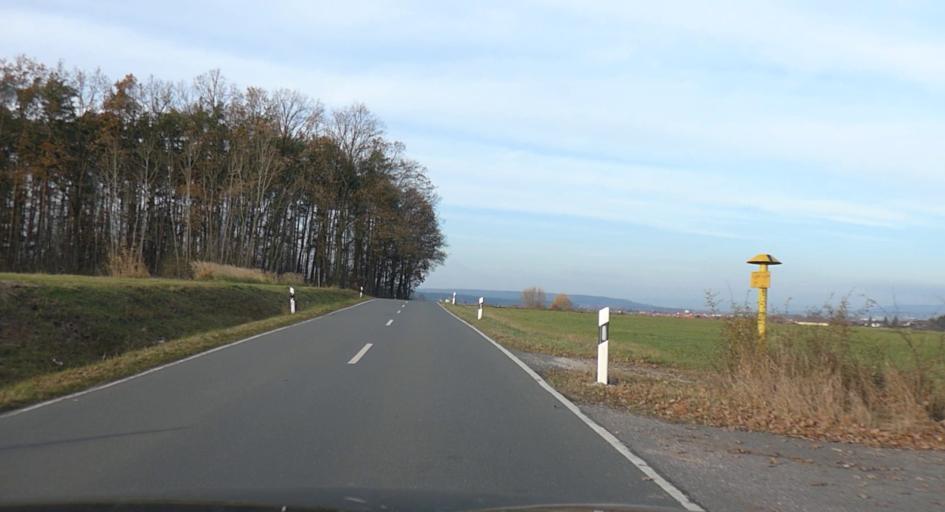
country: DE
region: Bavaria
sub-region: Regierungsbezirk Mittelfranken
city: Baiersdorf
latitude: 49.6359
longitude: 11.0387
